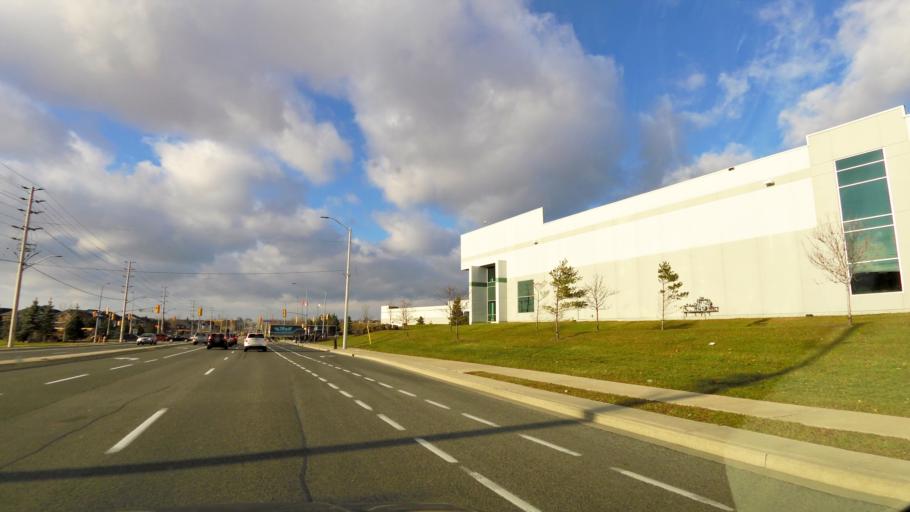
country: CA
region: Ontario
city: Mississauga
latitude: 43.6257
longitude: -79.7020
